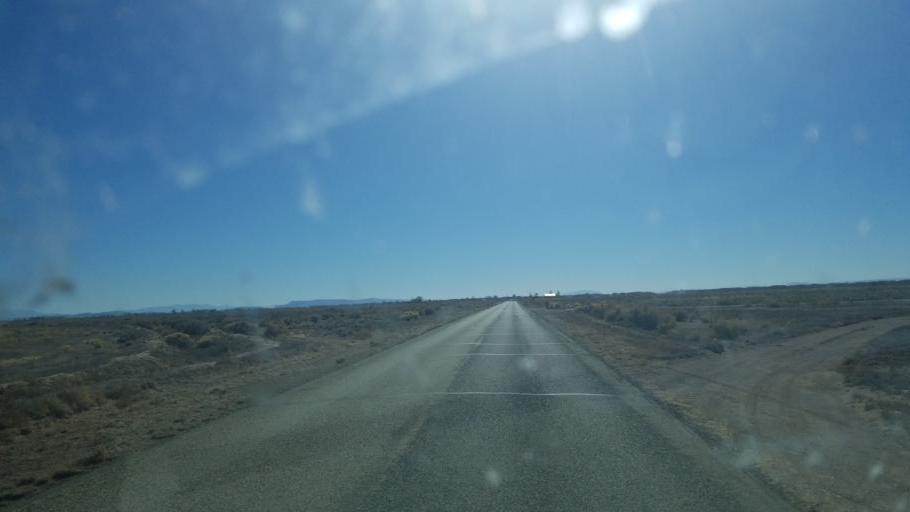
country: US
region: Colorado
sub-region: Alamosa County
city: Alamosa
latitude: 37.5700
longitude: -105.9289
